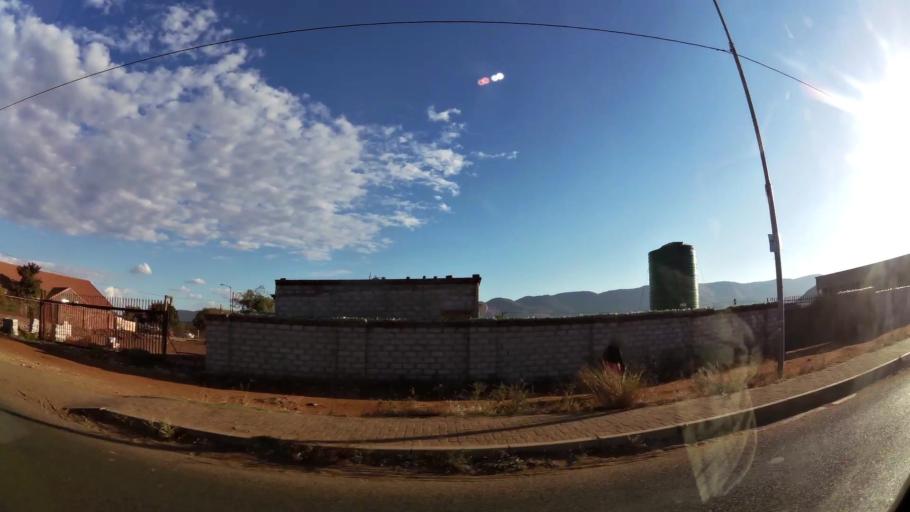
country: ZA
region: Limpopo
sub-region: Waterberg District Municipality
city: Mokopane
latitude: -24.1638
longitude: 28.9923
